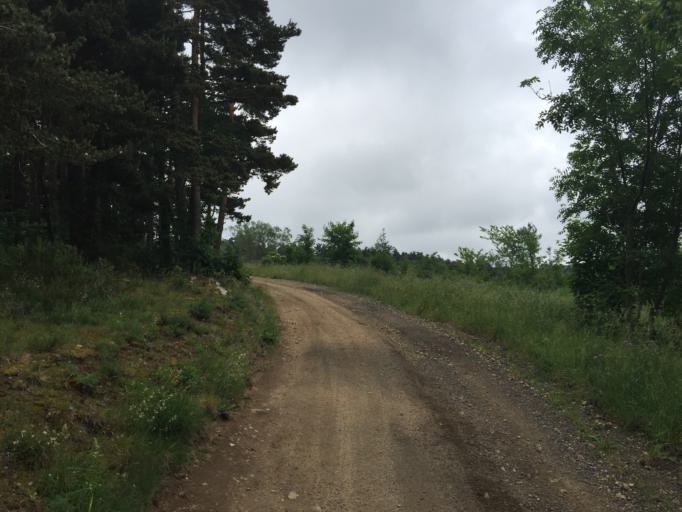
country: FR
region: Auvergne
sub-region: Departement de la Haute-Loire
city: Yssingeaux
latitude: 45.1355
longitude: 4.1587
